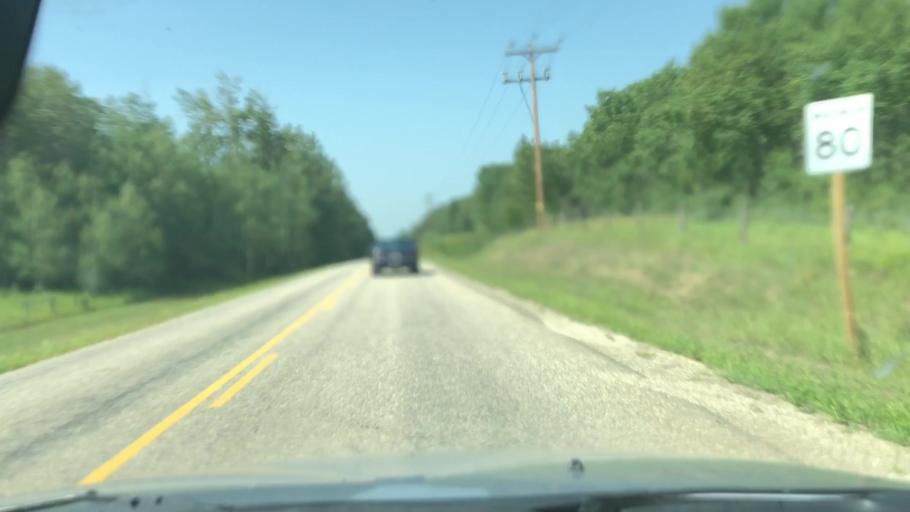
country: CA
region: Alberta
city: Devon
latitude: 53.4252
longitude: -113.7890
